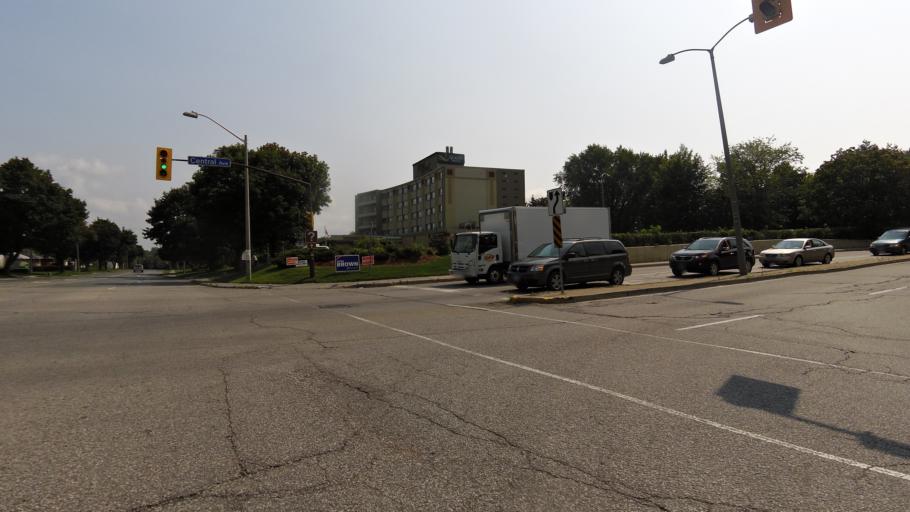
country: CA
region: Ontario
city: Brockville
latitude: 44.5978
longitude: -75.6969
